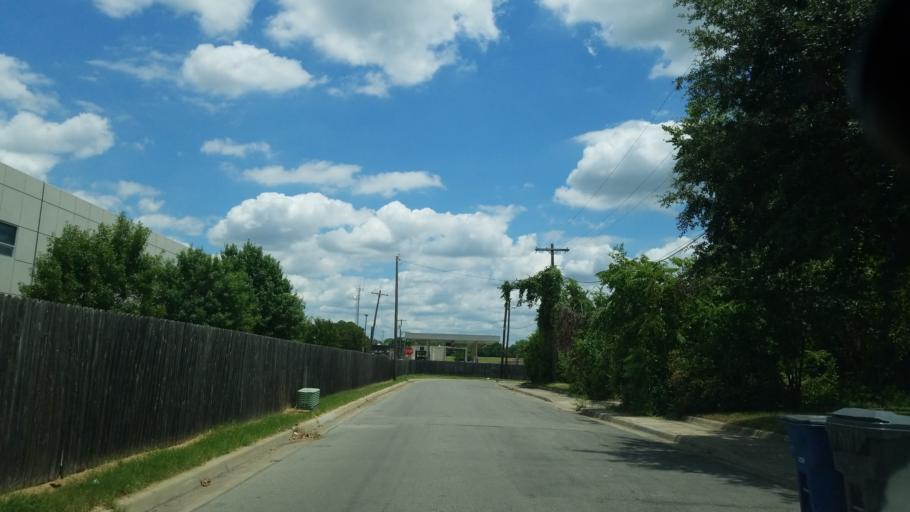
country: US
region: Texas
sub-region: Dallas County
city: Dallas
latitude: 32.7376
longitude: -96.7518
